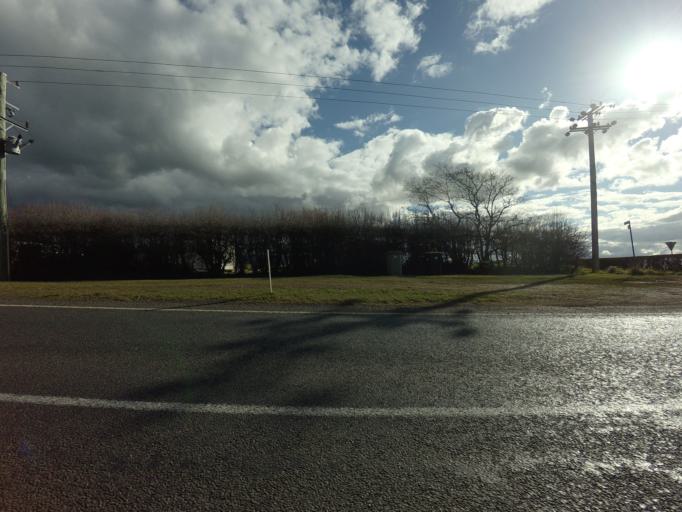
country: AU
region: Tasmania
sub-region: Northern Midlands
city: Longford
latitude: -41.7025
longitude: 147.0769
